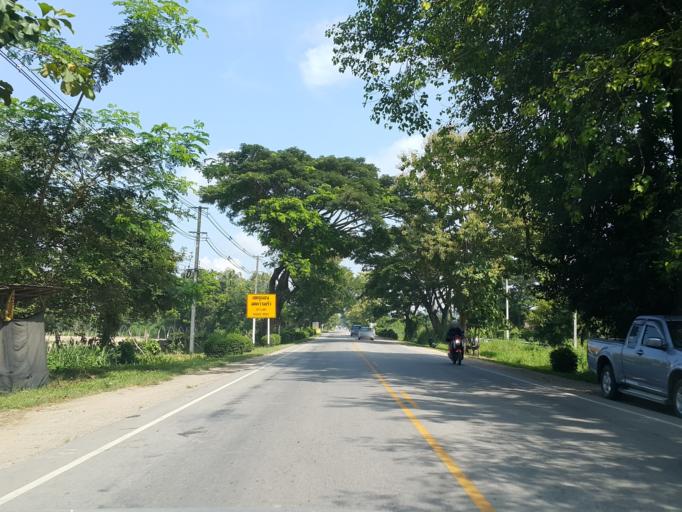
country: TH
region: Chiang Mai
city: San Sai
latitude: 18.9346
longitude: 98.9881
